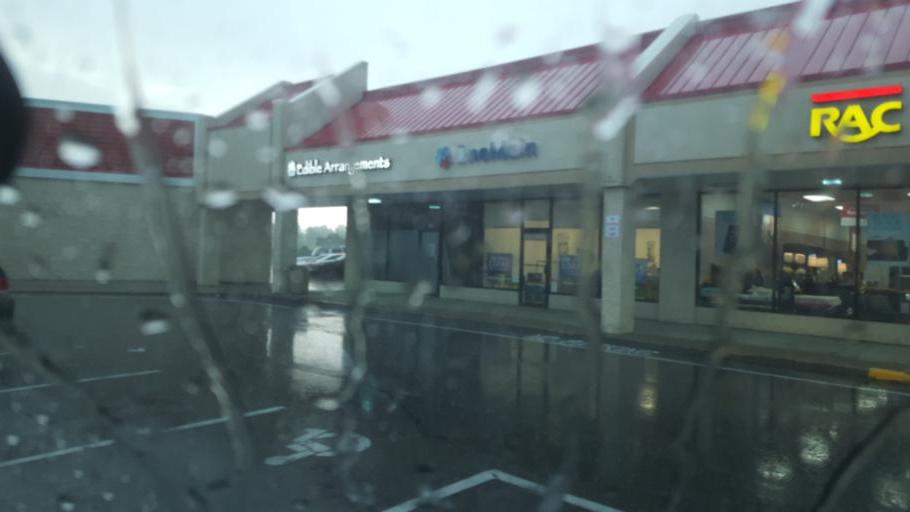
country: US
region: Ohio
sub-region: Richland County
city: Ontario
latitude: 40.7671
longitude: -82.5872
